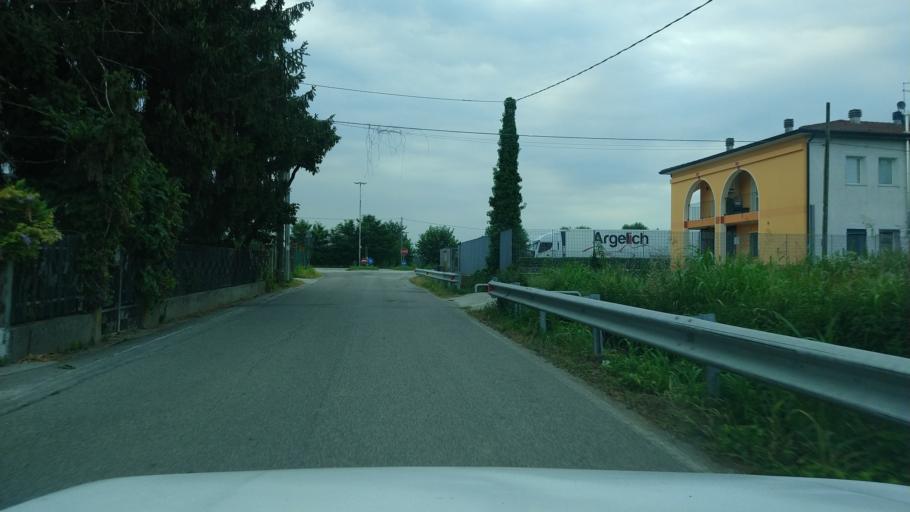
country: IT
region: Veneto
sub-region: Provincia di Vicenza
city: Schiavon
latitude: 45.7111
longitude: 11.6483
